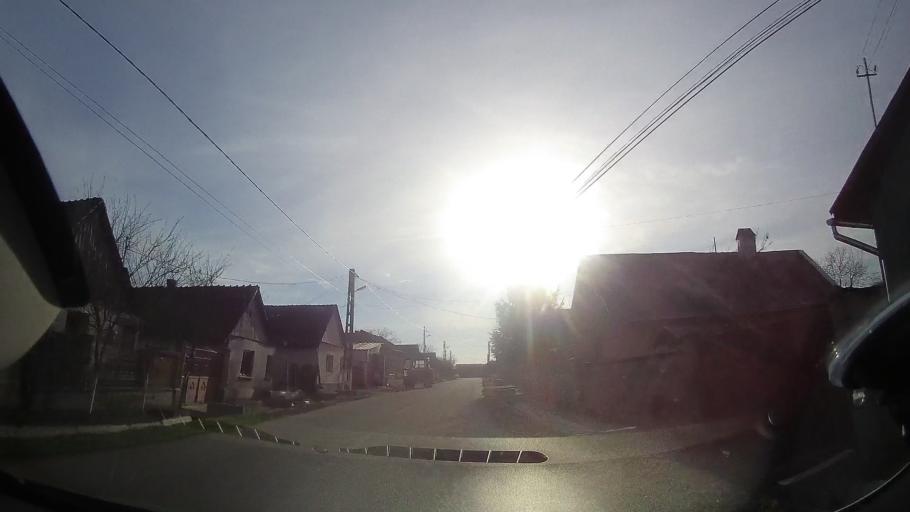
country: RO
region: Bihor
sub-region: Comuna Sarbi
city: Sarbi
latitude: 47.2070
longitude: 22.1304
